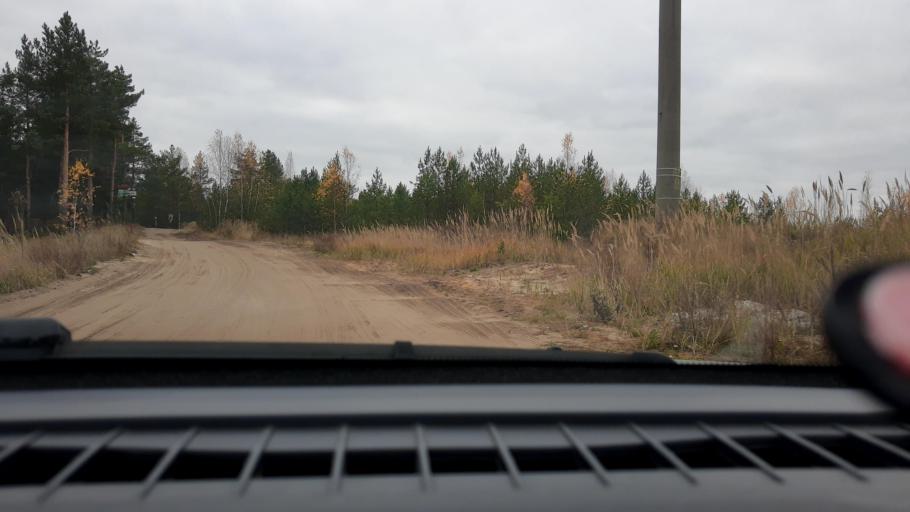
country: RU
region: Nizjnij Novgorod
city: Lukino
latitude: 56.3881
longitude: 43.6485
